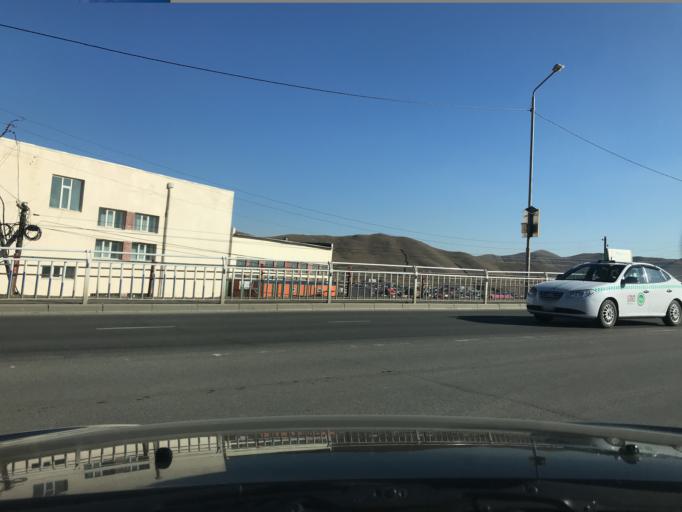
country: MN
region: Ulaanbaatar
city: Ulaanbaatar
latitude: 47.9950
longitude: 106.9257
